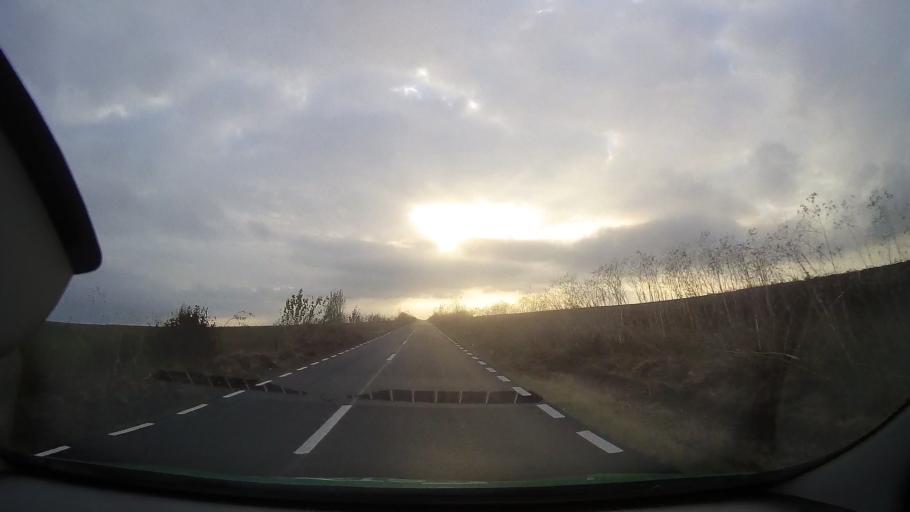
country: RO
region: Constanta
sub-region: Comuna Deleni
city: Deleni
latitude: 44.0747
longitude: 27.9888
